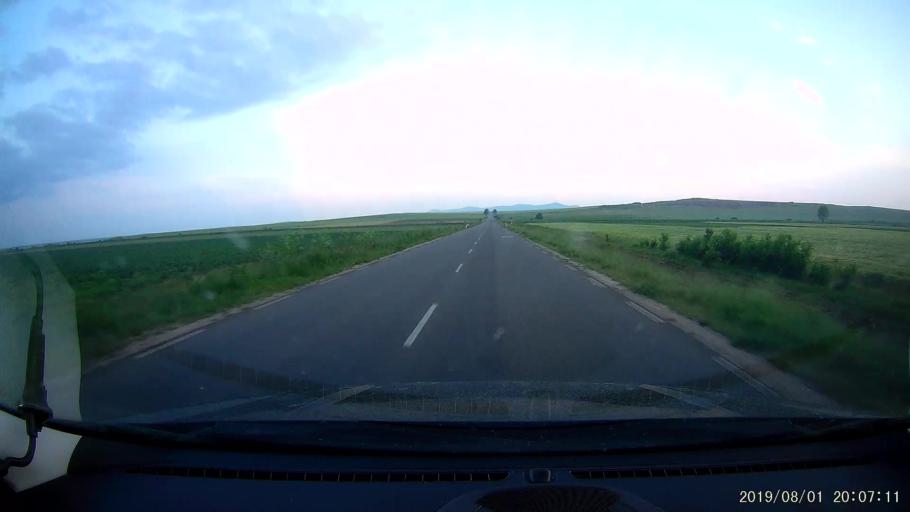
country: BG
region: Yambol
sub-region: Obshtina Yambol
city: Yambol
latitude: 42.5259
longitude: 26.5644
